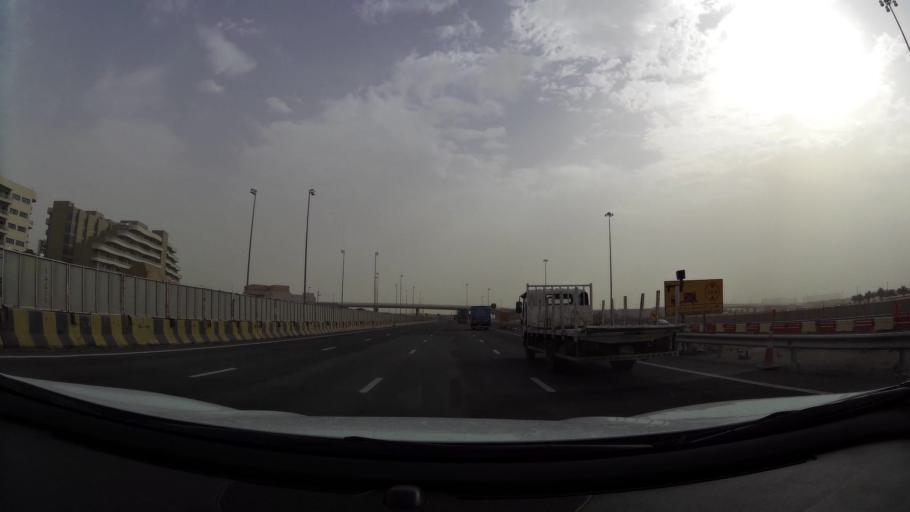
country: AE
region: Abu Dhabi
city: Abu Dhabi
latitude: 24.4485
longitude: 54.6129
